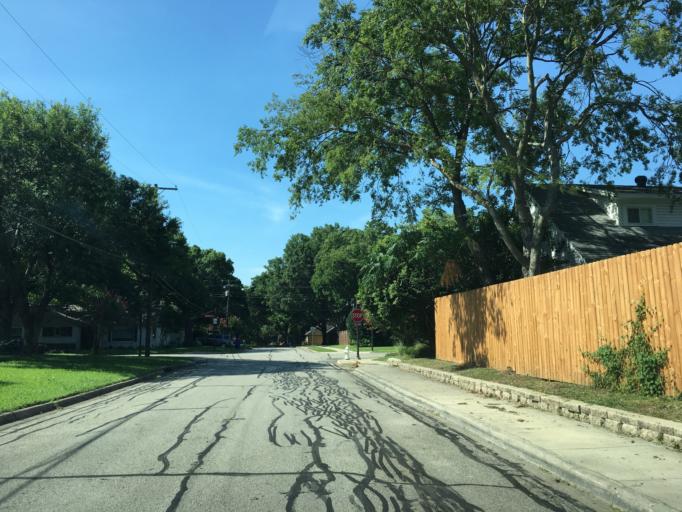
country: US
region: Texas
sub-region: Dallas County
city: Farmers Branch
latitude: 32.9188
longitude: -96.8792
